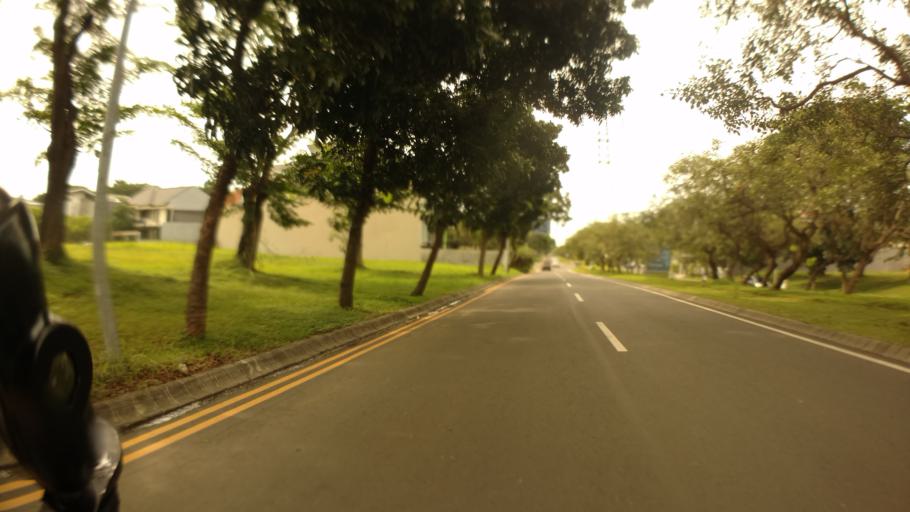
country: ID
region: East Java
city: Driyorejo
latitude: -7.2896
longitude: 112.6478
